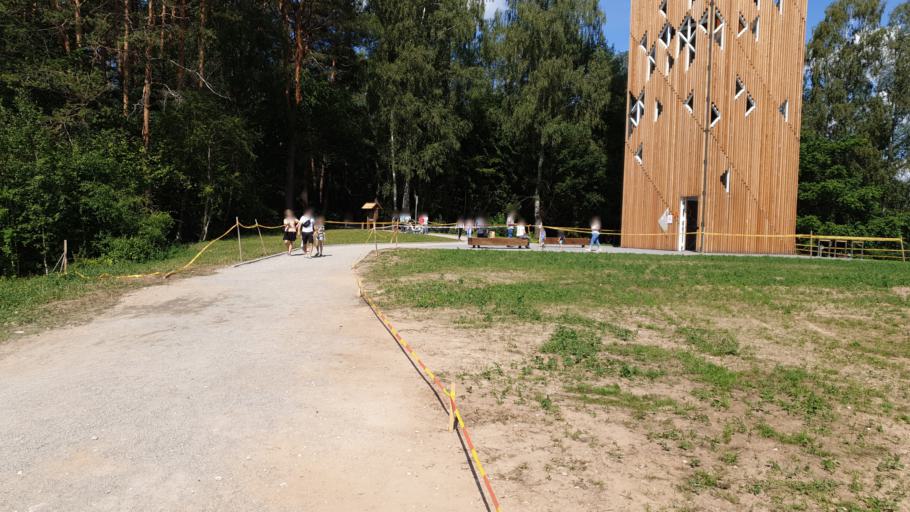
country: LT
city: Birstonas
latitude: 54.6035
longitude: 24.0133
